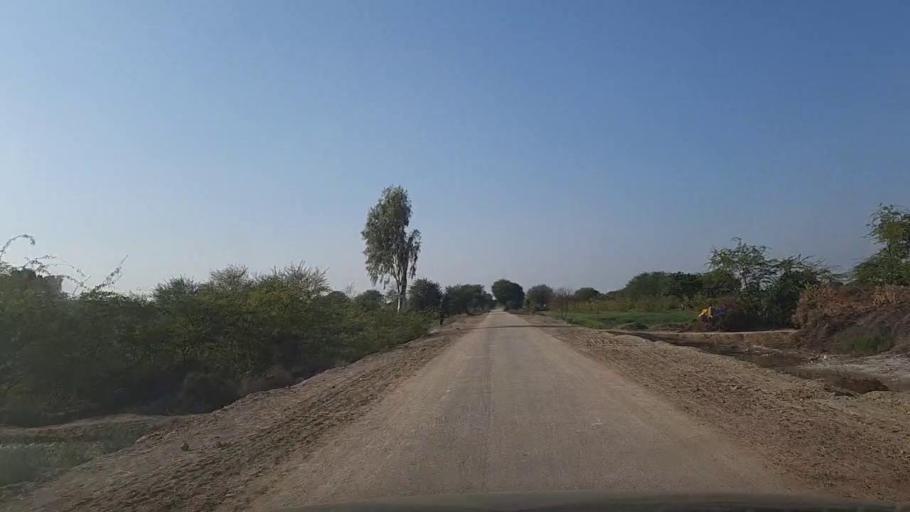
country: PK
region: Sindh
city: Digri
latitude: 25.0241
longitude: 69.2285
